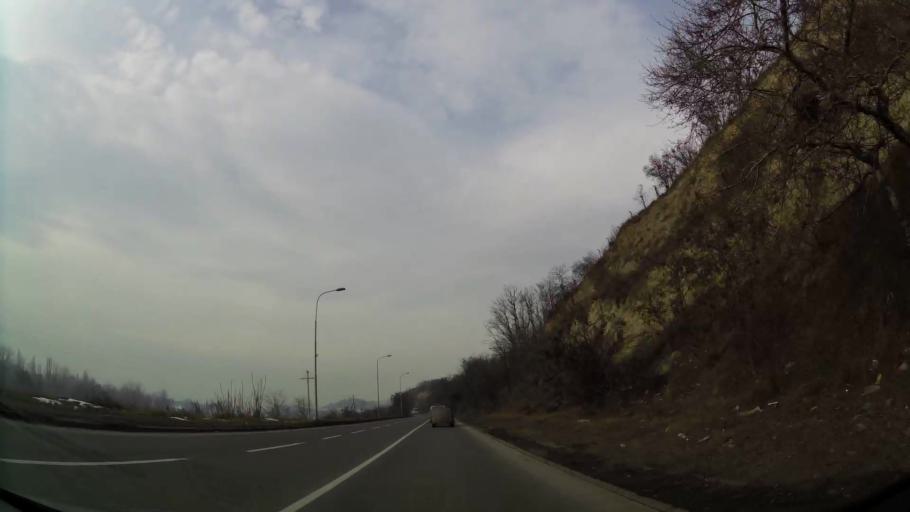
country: MK
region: Karpos
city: Skopje
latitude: 42.0131
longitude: 21.4204
